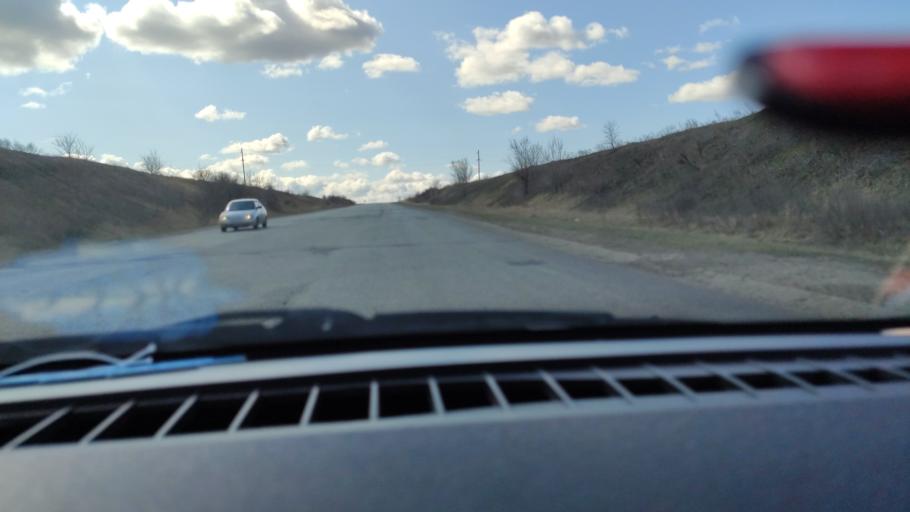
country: RU
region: Samara
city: Varlamovo
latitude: 53.0890
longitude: 48.3551
